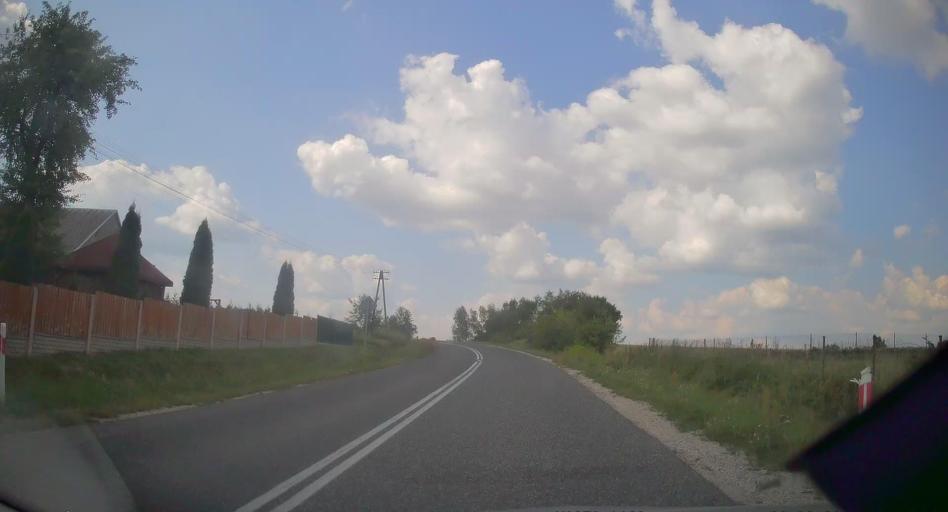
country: PL
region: Swietokrzyskie
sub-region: Powiat kielecki
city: Lopuszno
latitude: 50.9107
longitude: 20.2451
